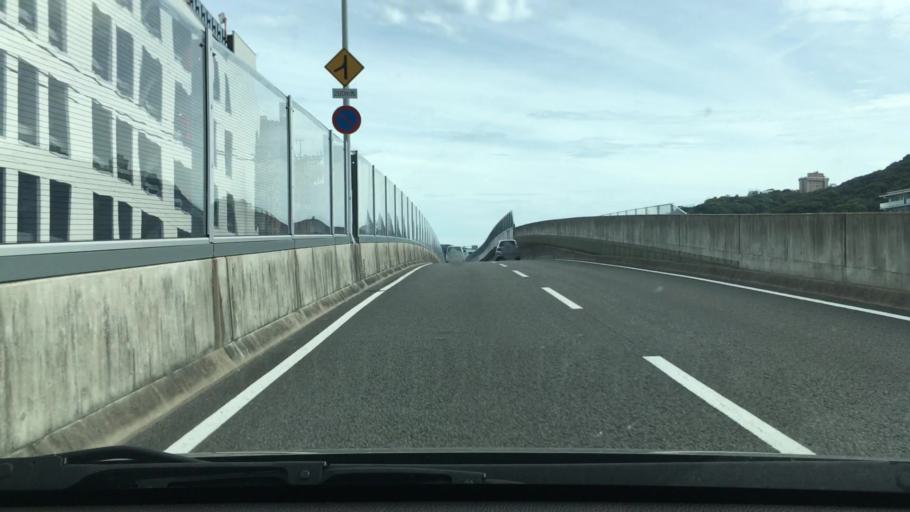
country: JP
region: Nagasaki
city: Nagasaki-shi
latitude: 32.7645
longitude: 129.8622
